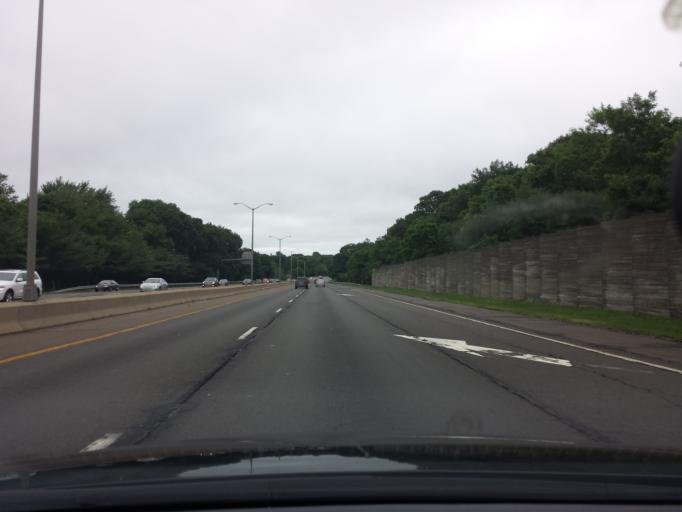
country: US
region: Connecticut
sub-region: Middlesex County
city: Old Saybrook Center
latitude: 41.3213
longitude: -72.3368
